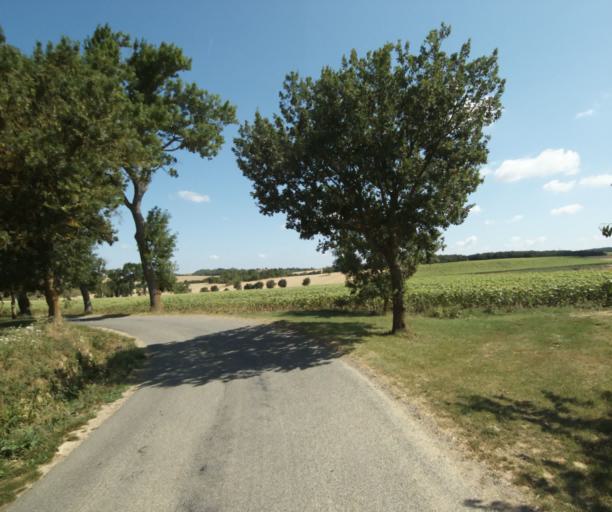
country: FR
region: Midi-Pyrenees
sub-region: Departement de la Haute-Garonne
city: Auriac-sur-Vendinelle
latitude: 43.4519
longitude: 1.7897
